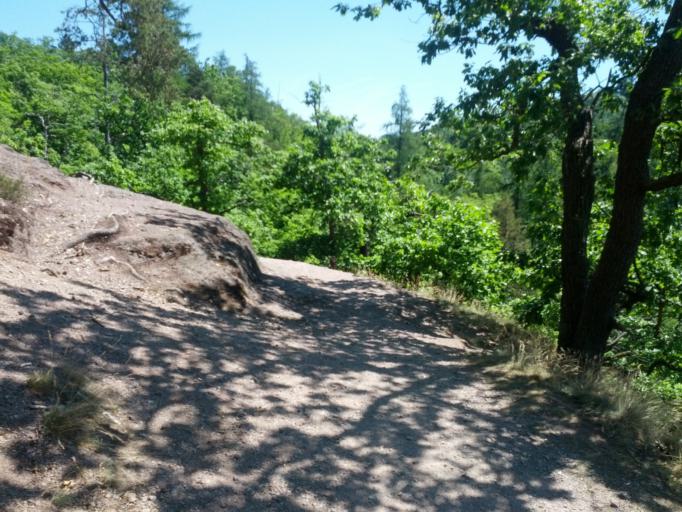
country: DE
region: Thuringia
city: Eisenach
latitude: 50.9701
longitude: 10.3052
